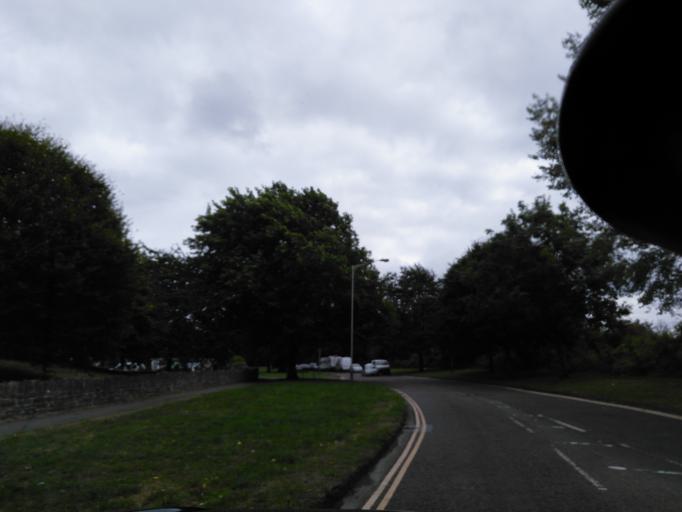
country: GB
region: England
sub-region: Wiltshire
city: Bradford-on-Avon
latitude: 51.3370
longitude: -2.2500
